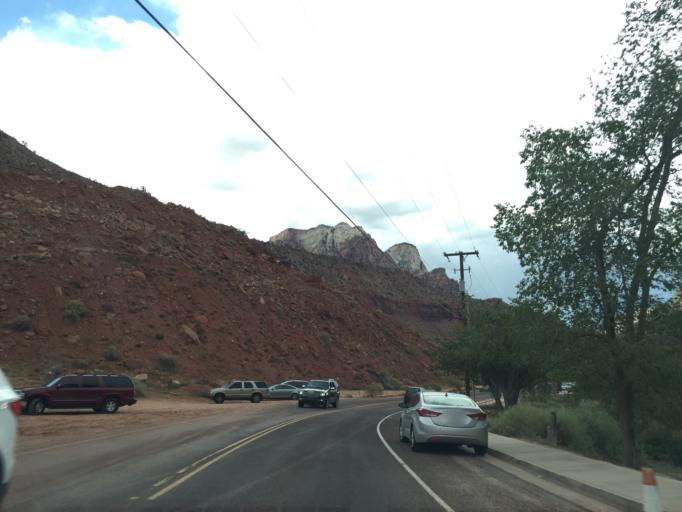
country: US
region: Utah
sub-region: Washington County
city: Hildale
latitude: 37.1959
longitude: -112.9927
